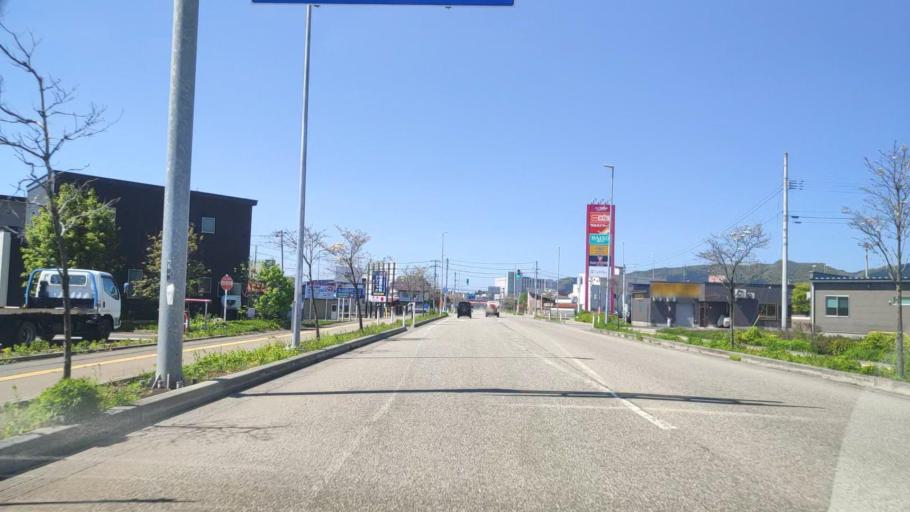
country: JP
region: Akita
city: Omagari
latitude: 39.4694
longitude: 140.4843
